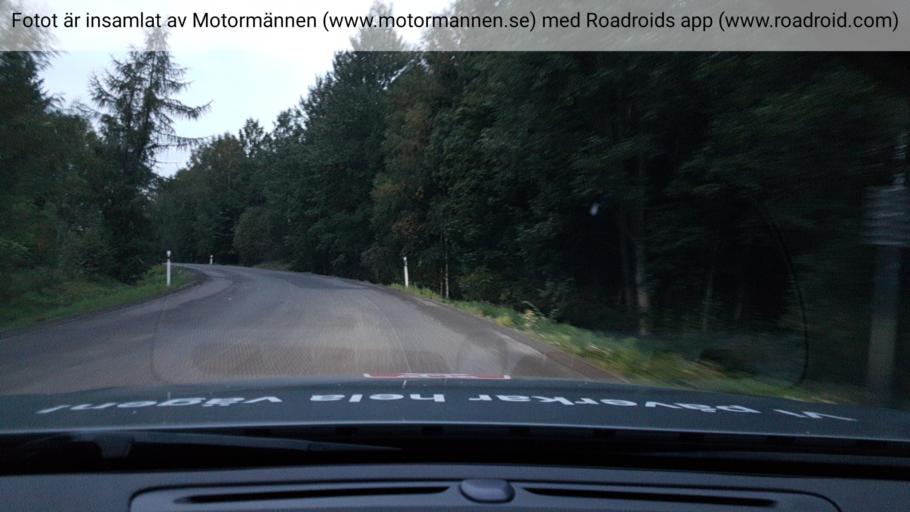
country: SE
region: OErebro
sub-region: Nora Kommun
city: As
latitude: 59.4631
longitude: 14.8646
